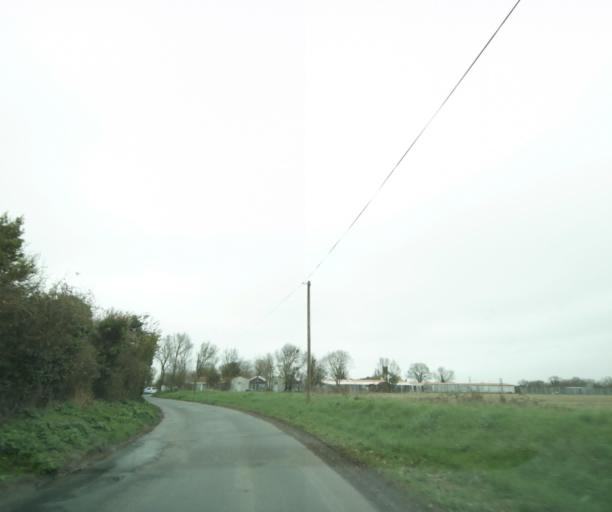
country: FR
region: Poitou-Charentes
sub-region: Departement de la Charente-Maritime
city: Lagord
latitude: 46.1826
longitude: -1.1379
